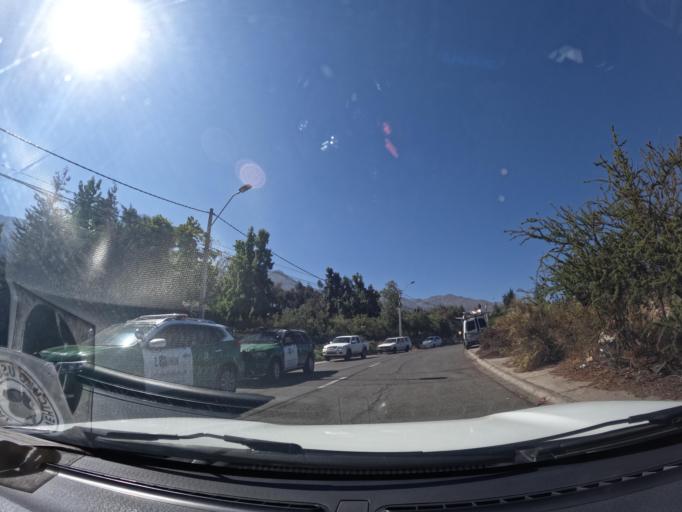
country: CL
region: Santiago Metropolitan
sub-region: Provincia de Santiago
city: Villa Presidente Frei, Nunoa, Santiago, Chile
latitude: -33.4724
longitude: -70.5208
